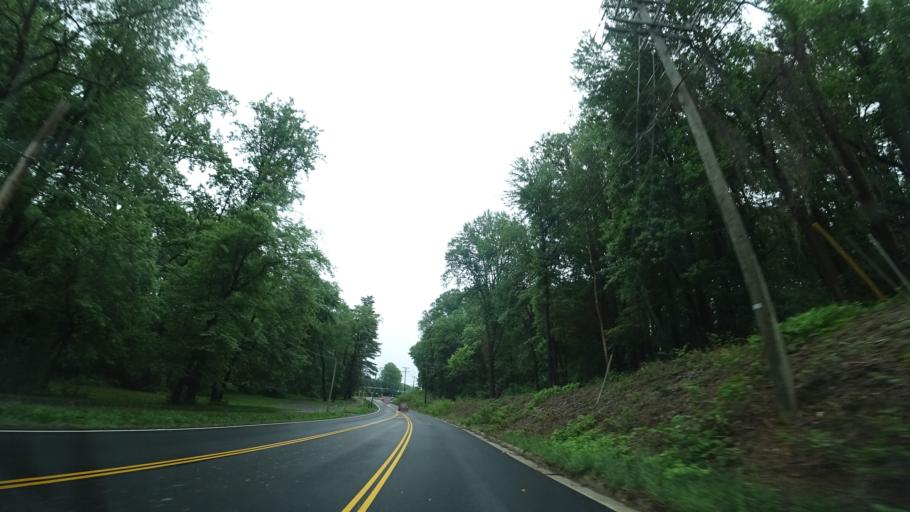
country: US
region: Virginia
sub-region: Fairfax County
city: Pimmit Hills
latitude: 38.9348
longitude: -77.2057
